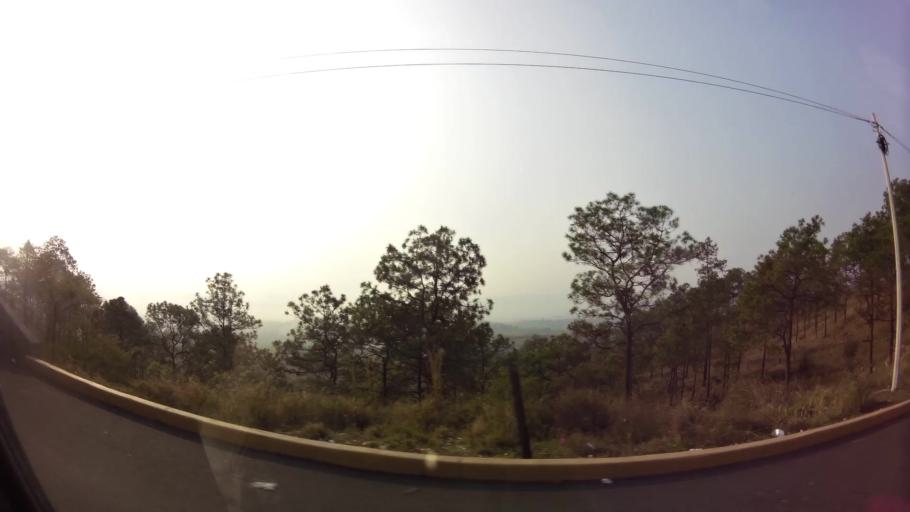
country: HN
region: Francisco Morazan
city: Zambrano
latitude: 14.2372
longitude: -87.3873
